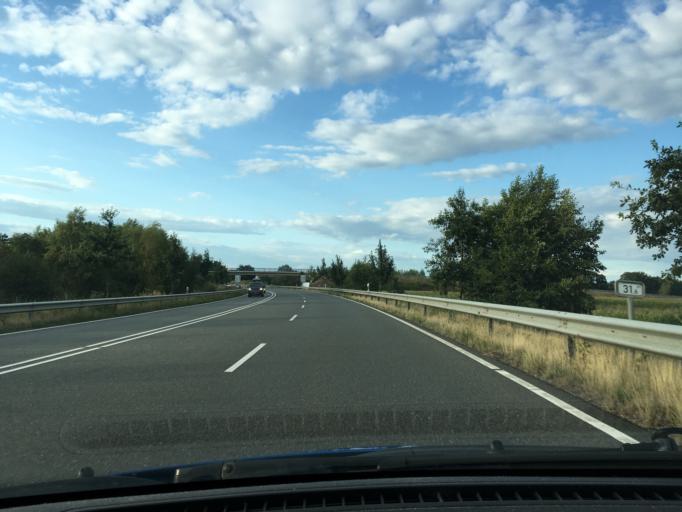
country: DE
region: Lower Saxony
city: Adelheidsdorf
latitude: 52.5411
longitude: 10.0715
